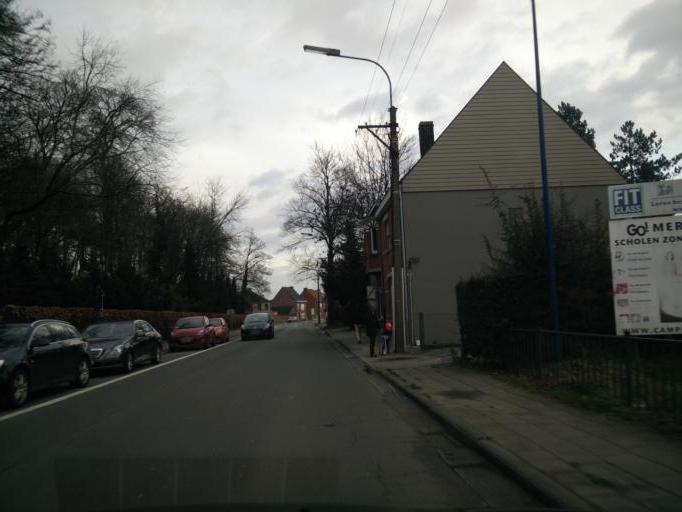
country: BE
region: Flanders
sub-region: Provincie Oost-Vlaanderen
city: Merelbeke
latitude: 50.9993
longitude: 3.7450
